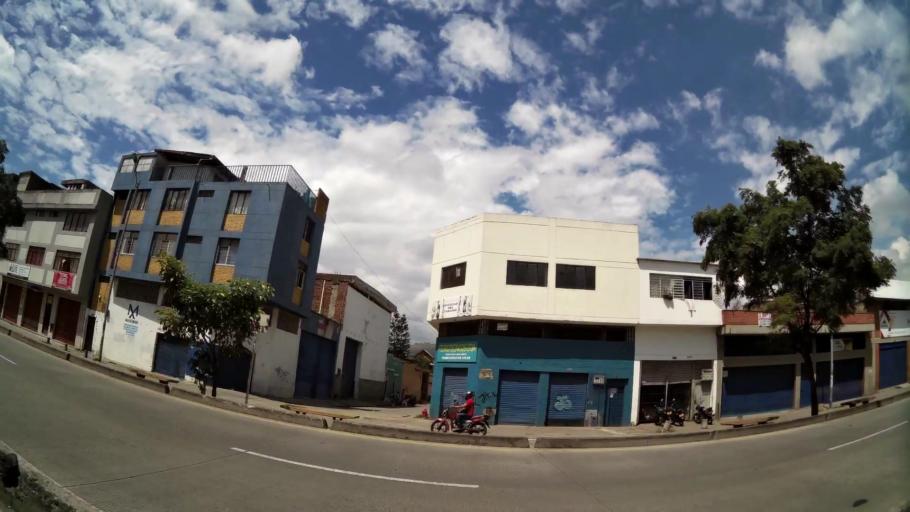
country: CO
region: Valle del Cauca
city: Cali
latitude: 3.4455
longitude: -76.5267
